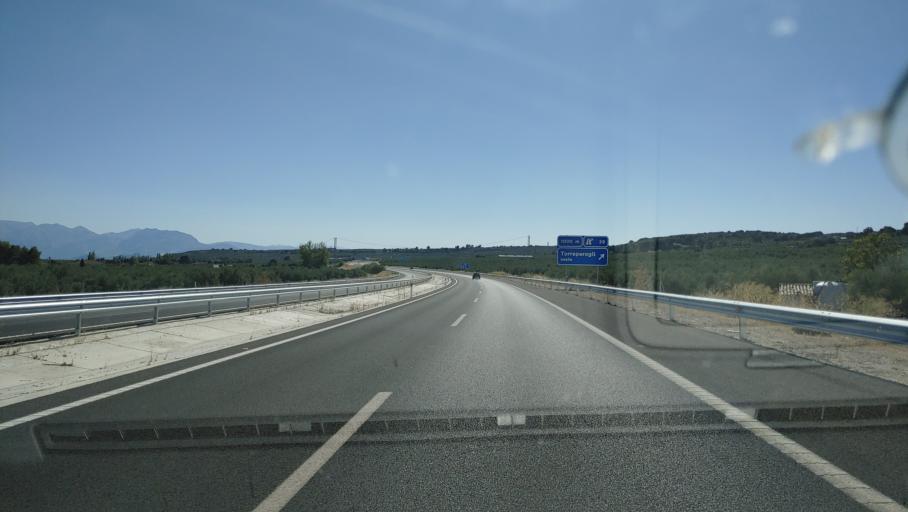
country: ES
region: Andalusia
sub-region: Provincia de Jaen
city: Sabiote
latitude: 38.0420
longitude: -3.3185
